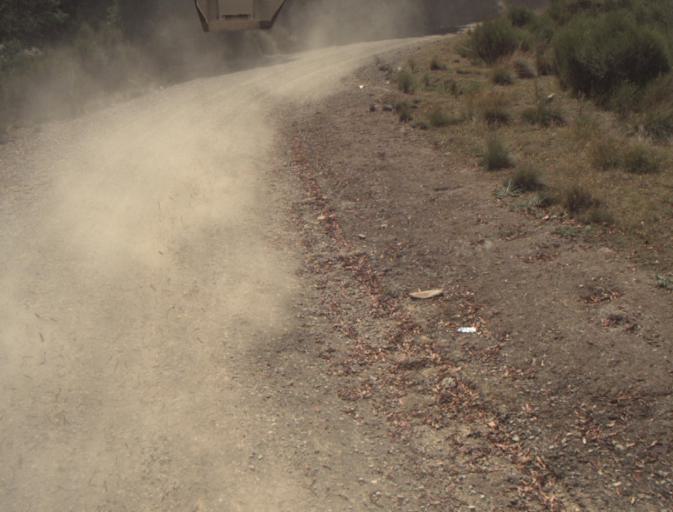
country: AU
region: Tasmania
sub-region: Dorset
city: Scottsdale
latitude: -41.3148
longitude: 147.4640
